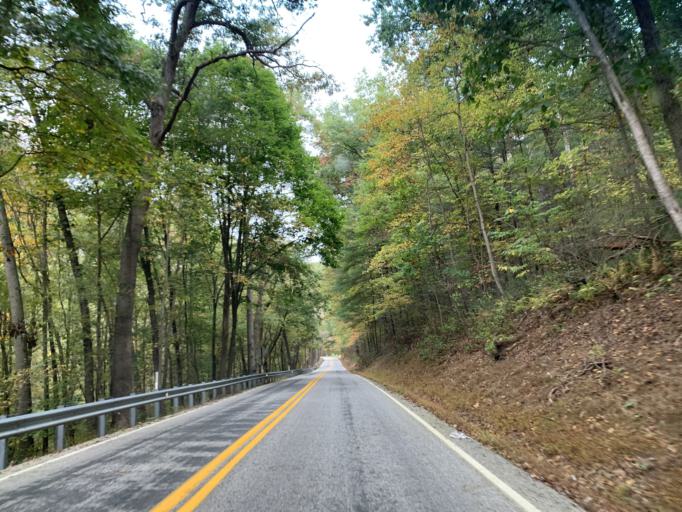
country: US
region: Pennsylvania
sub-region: York County
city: Susquehanna Trails
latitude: 39.7638
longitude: -76.4279
